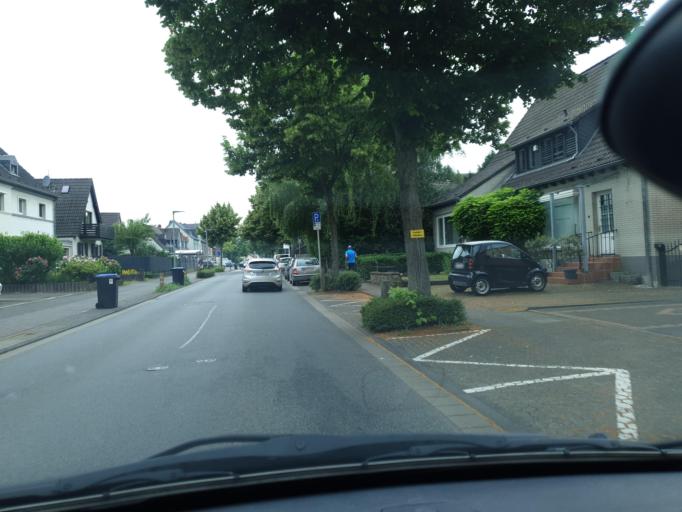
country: DE
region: North Rhine-Westphalia
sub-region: Regierungsbezirk Koln
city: Hurth
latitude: 50.8887
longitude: 6.8411
